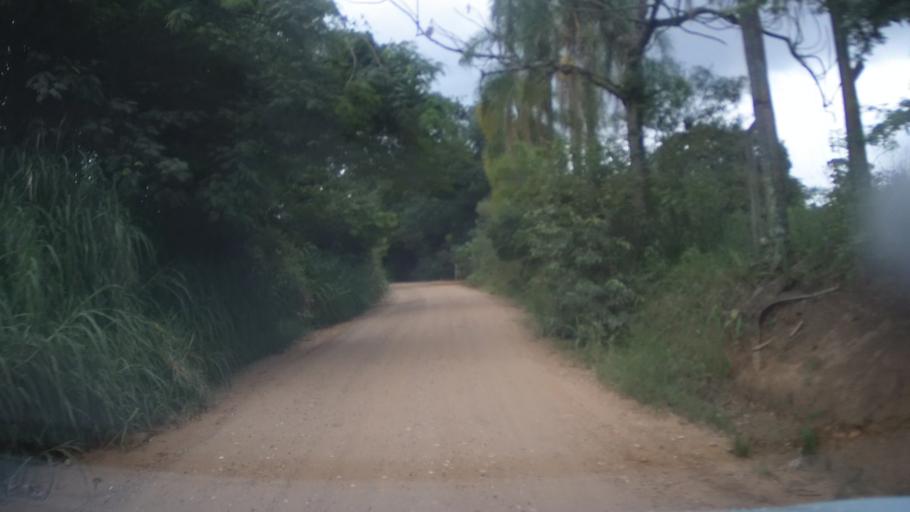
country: BR
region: Sao Paulo
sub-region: Itupeva
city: Itupeva
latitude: -23.1991
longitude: -47.0161
